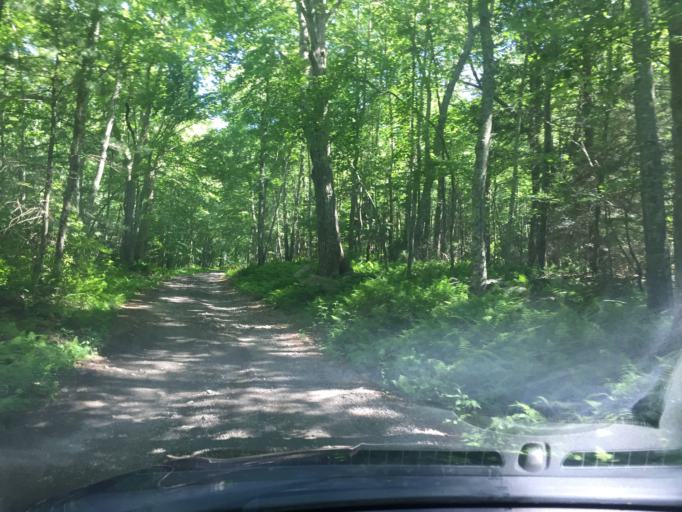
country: US
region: Rhode Island
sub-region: Washington County
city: Hopkinton
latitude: 41.5214
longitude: -71.8018
